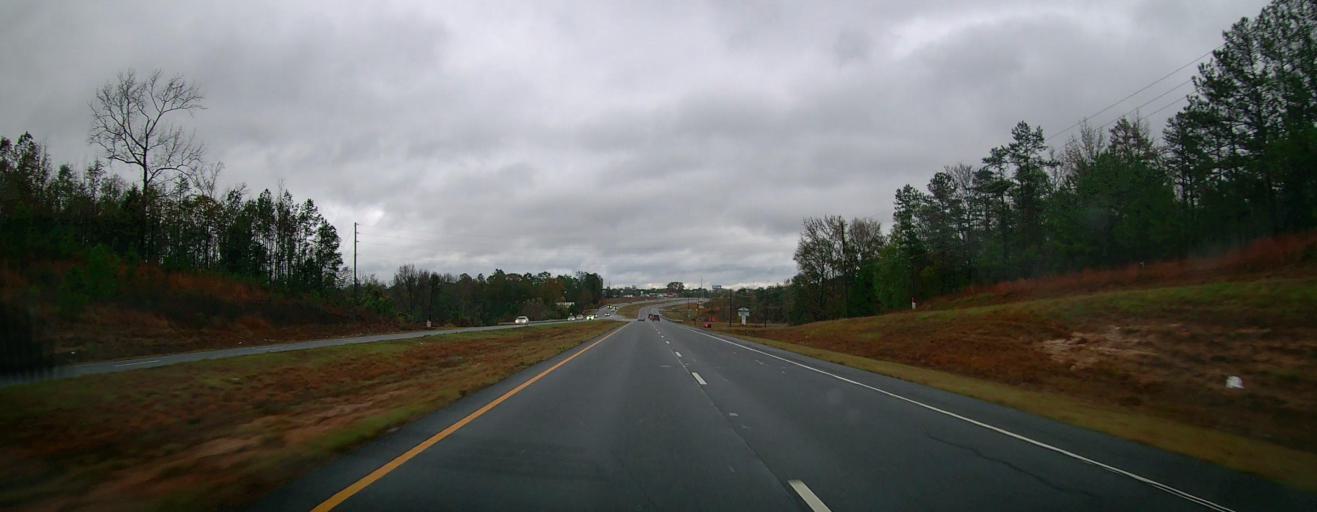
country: US
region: Georgia
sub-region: Jackson County
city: Commerce
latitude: 34.1758
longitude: -83.4438
